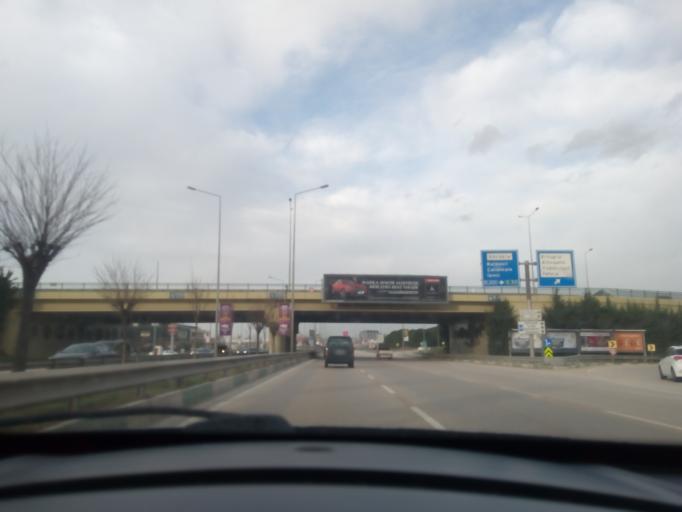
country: TR
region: Bursa
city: Cali
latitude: 40.2137
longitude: 28.9163
